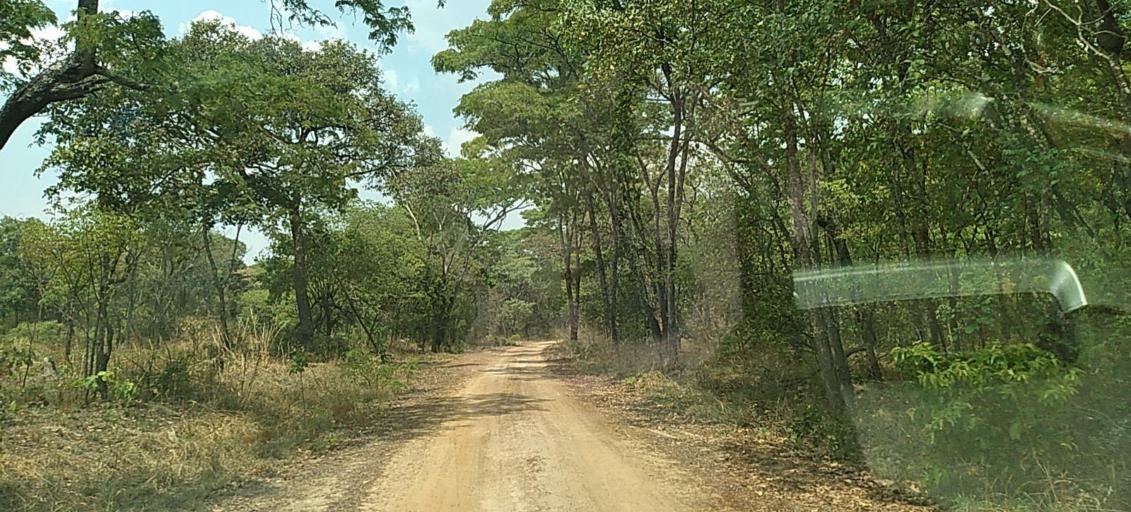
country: ZM
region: Copperbelt
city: Chingola
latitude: -12.7706
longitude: 27.6912
